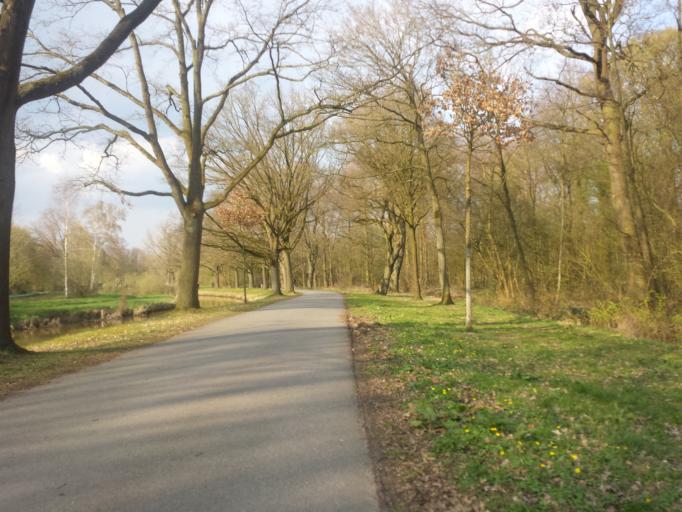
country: DE
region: Bremen
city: Bremen
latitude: 53.1079
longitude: 8.8243
